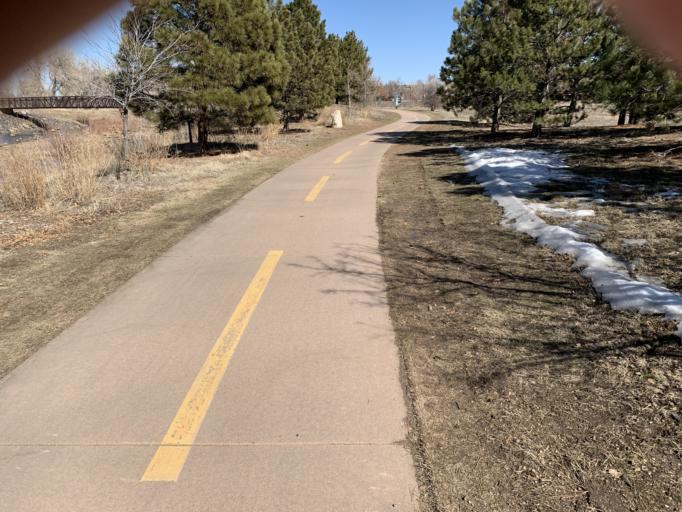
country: US
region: Colorado
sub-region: Arapahoe County
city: Littleton
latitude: 39.6140
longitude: -105.0240
